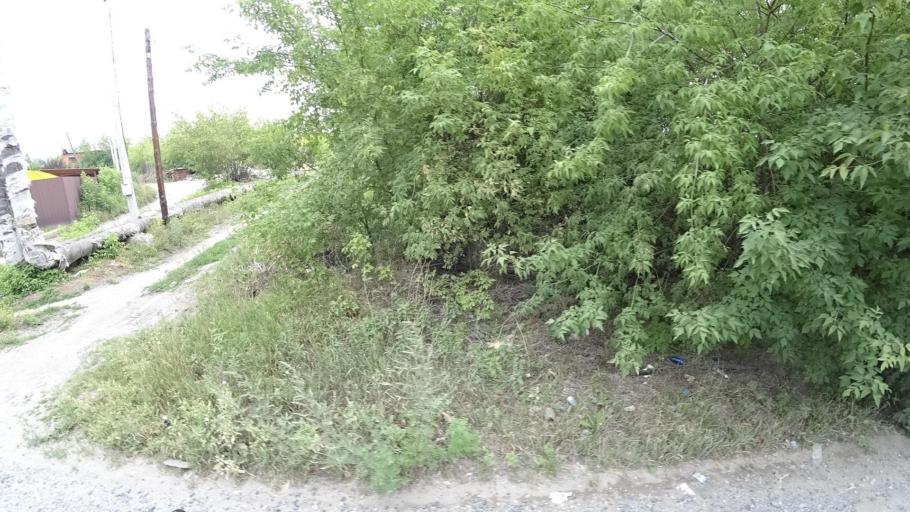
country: RU
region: Sverdlovsk
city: Kamyshlov
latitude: 56.8351
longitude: 62.7194
